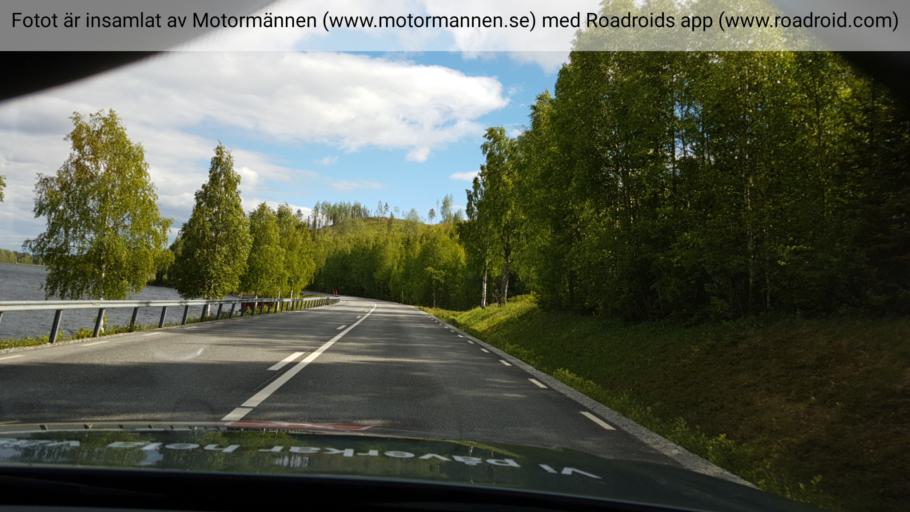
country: SE
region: Jaemtland
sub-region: Stroemsunds Kommun
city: Stroemsund
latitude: 64.1749
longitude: 15.6612
